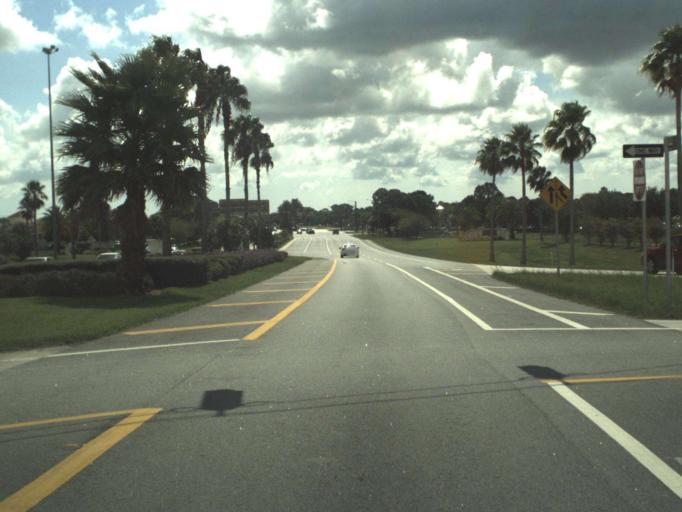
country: US
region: Florida
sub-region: Saint Lucie County
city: Port Saint Lucie
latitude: 27.3113
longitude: -80.4113
